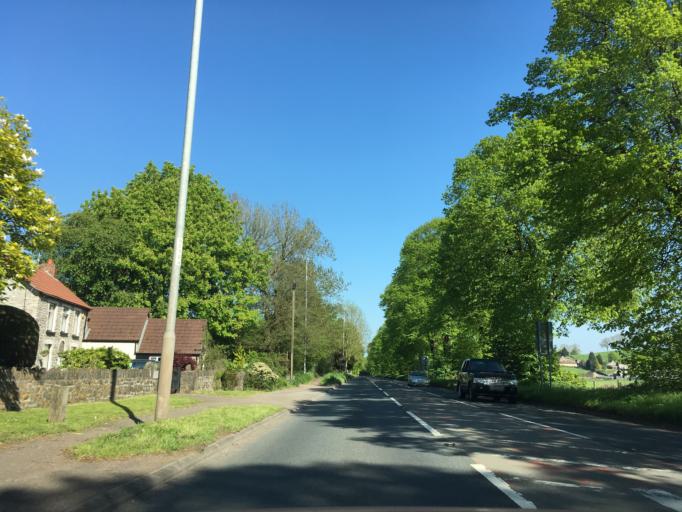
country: GB
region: Wales
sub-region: Newport
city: Llanvaches
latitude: 51.6159
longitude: -2.8428
